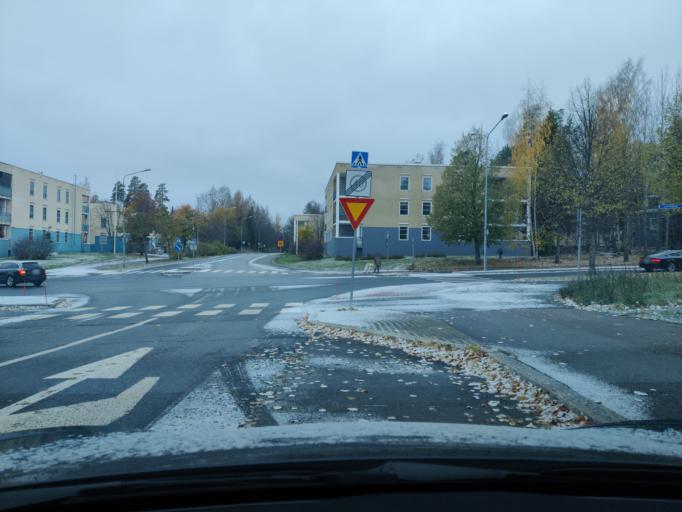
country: FI
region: Northern Savo
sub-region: Kuopio
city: Kuopio
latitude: 62.8392
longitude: 27.6361
